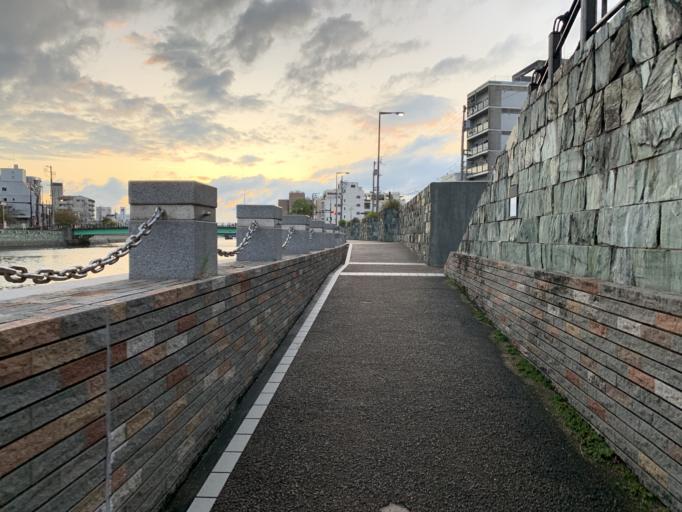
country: JP
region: Tokushima
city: Tokushima-shi
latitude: 34.0676
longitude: 134.5524
